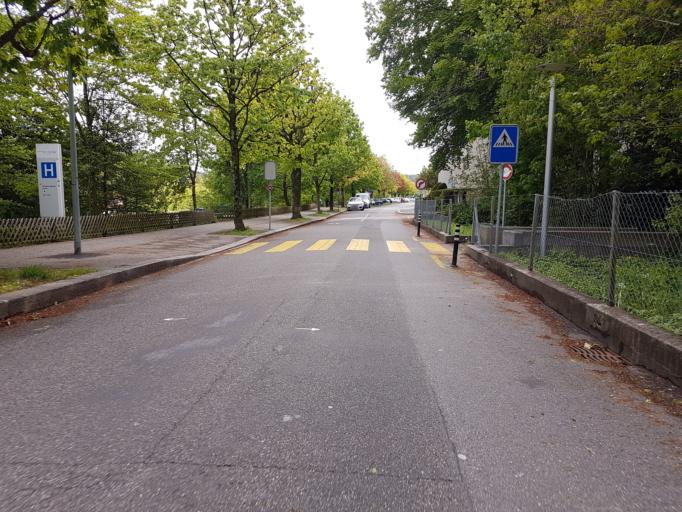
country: CH
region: Solothurn
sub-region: Bezirk Olten
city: Olten
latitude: 47.3554
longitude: 7.9058
